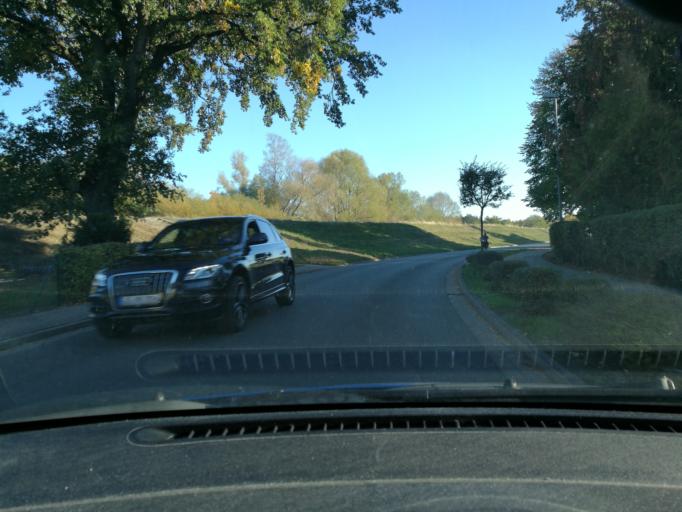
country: DE
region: Lower Saxony
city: Bleckede
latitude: 53.2879
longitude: 10.7384
